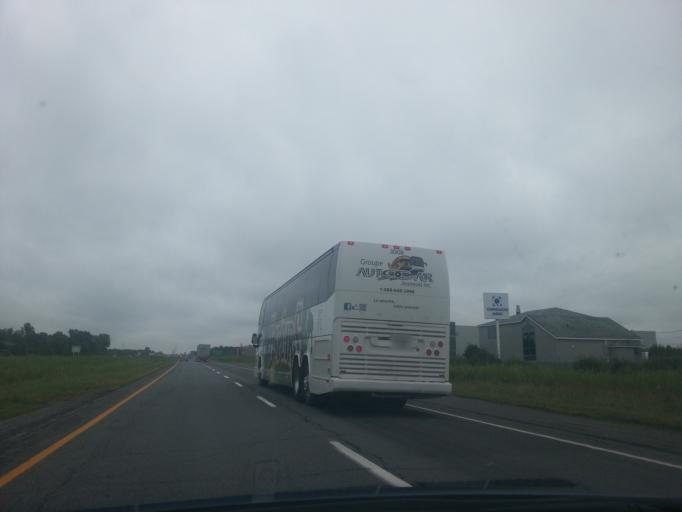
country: CA
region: Quebec
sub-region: Mauricie
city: Saint-Germain-de-Grantham
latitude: 45.8600
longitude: -72.5743
